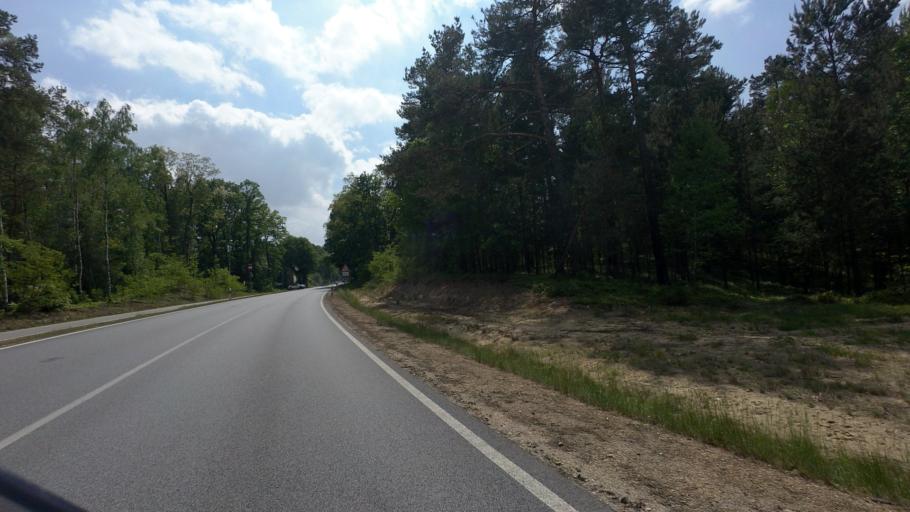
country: DE
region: Saxony
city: Rietschen
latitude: 51.4145
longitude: 14.7885
